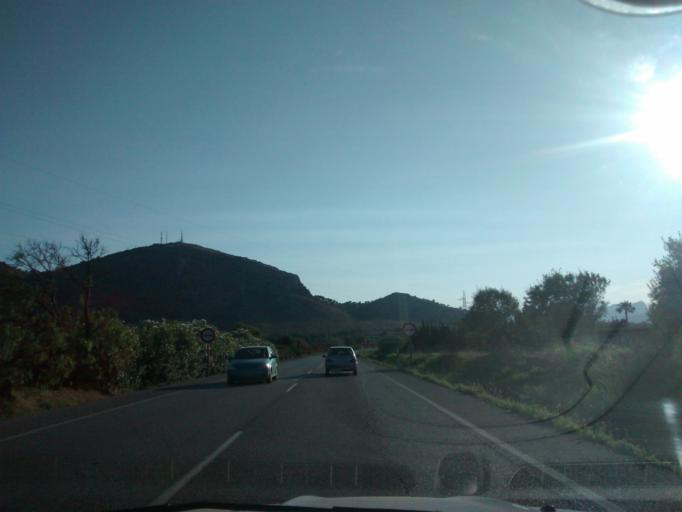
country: ES
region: Balearic Islands
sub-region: Illes Balears
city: Alcudia
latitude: 39.8429
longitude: 3.1101
